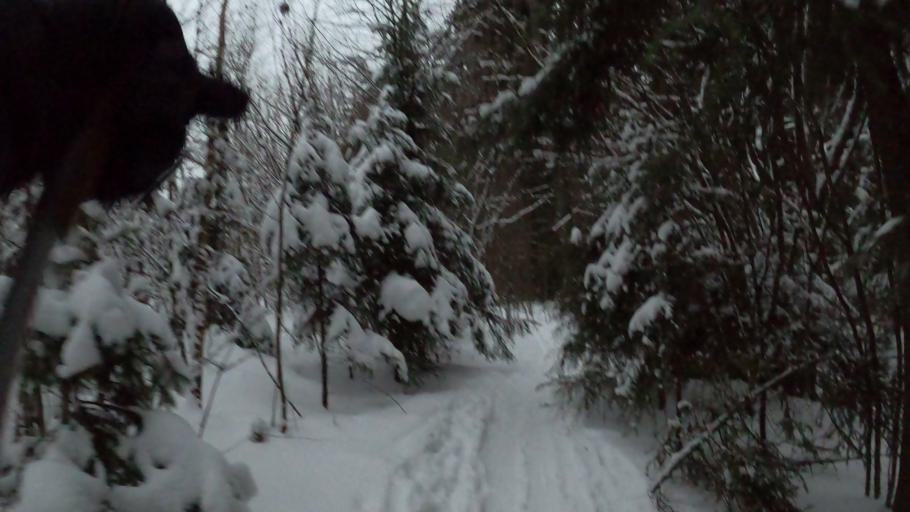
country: RU
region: Moskovskaya
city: Nakhabino
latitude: 55.8950
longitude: 37.2080
